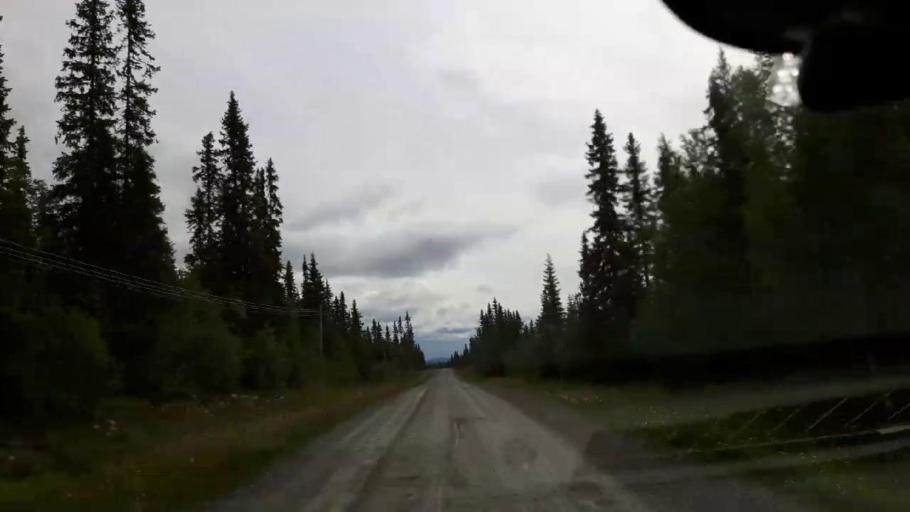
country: SE
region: Jaemtland
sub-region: Krokoms Kommun
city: Valla
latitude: 63.7260
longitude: 13.8442
